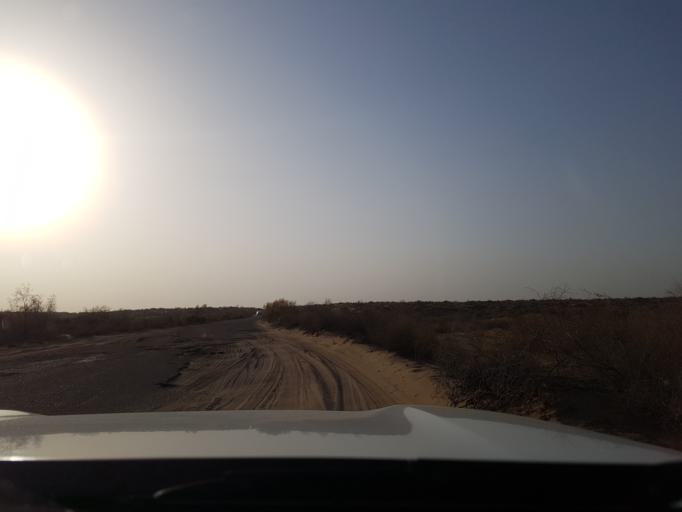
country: UZ
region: Xorazm
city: Hazorasp
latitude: 41.1731
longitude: 60.8186
